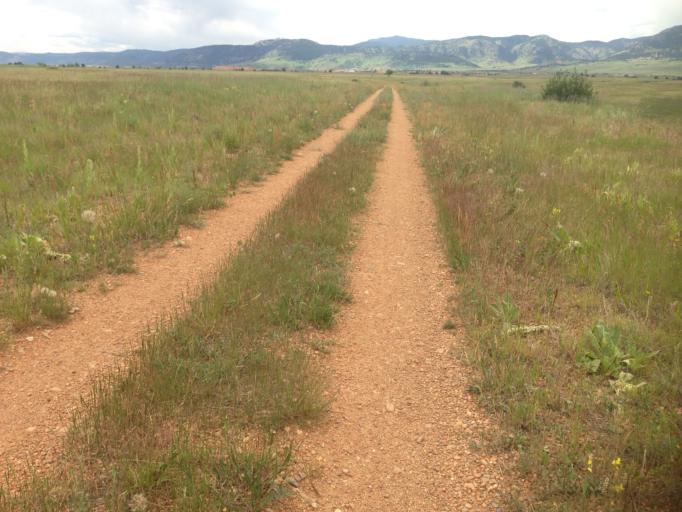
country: US
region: Colorado
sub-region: Boulder County
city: Superior
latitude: 39.9055
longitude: -105.2050
